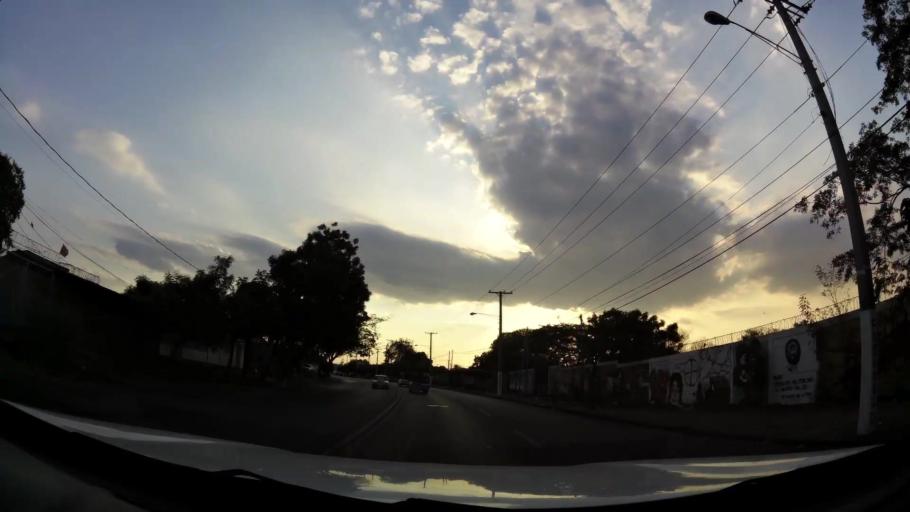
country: NI
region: Managua
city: Managua
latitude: 12.1464
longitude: -86.2469
